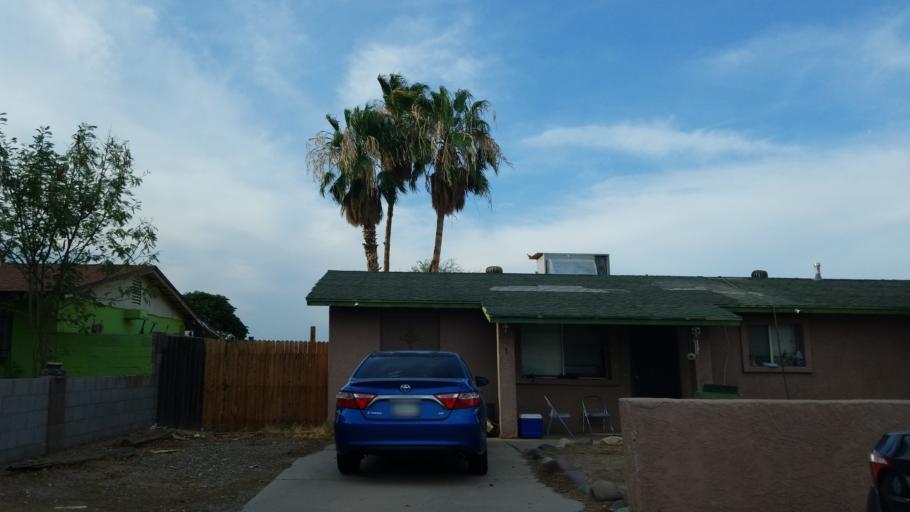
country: US
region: Arizona
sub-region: Maricopa County
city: Guadalupe
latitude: 33.3728
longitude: -112.0286
